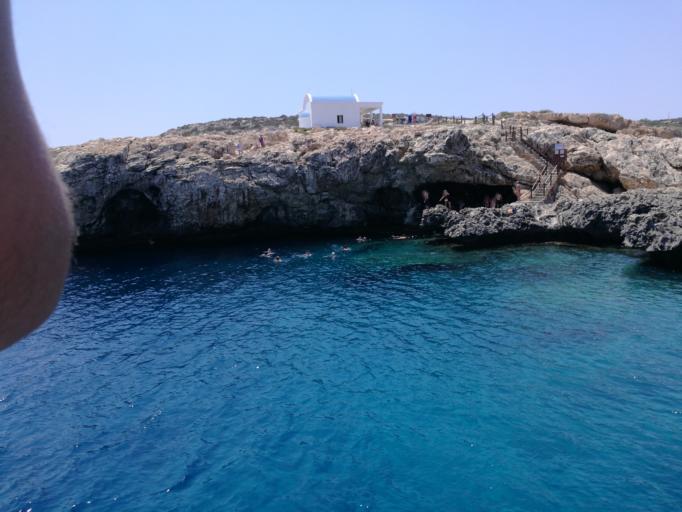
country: CY
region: Ammochostos
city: Protaras
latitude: 34.9761
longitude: 34.0769
